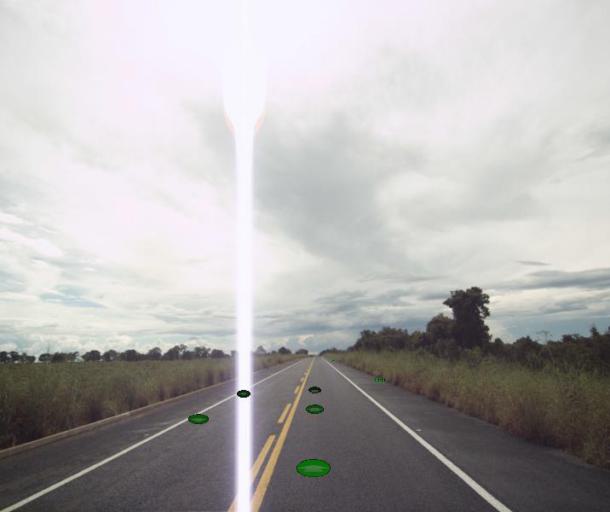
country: BR
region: Goias
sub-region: Sao Miguel Do Araguaia
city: Sao Miguel do Araguaia
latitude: -13.2782
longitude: -50.4979
